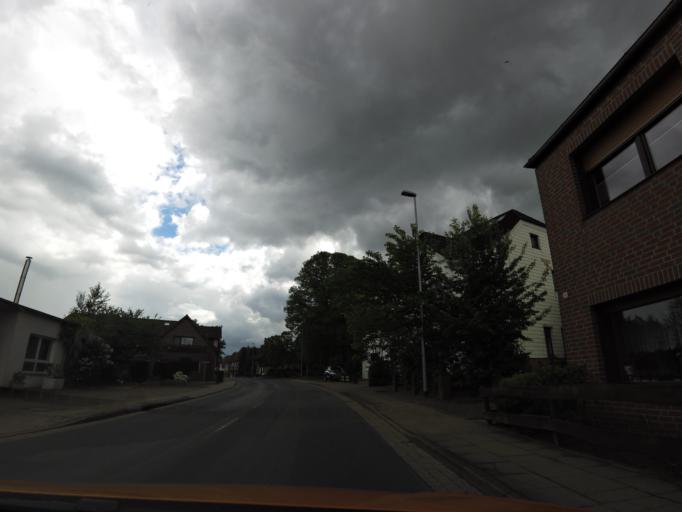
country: DE
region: Lower Saxony
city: Ganderkesee
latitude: 53.0998
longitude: 8.5338
